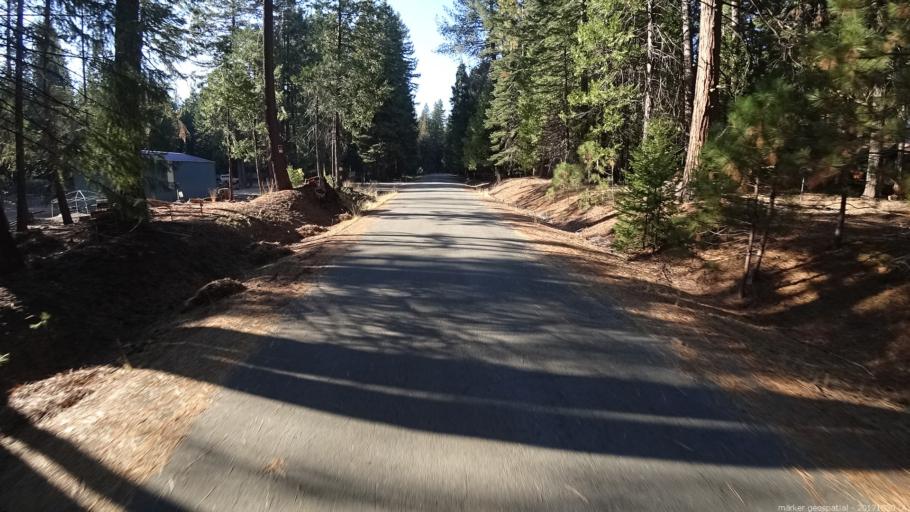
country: US
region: California
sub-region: Shasta County
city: Shingletown
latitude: 40.5530
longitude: -121.7293
